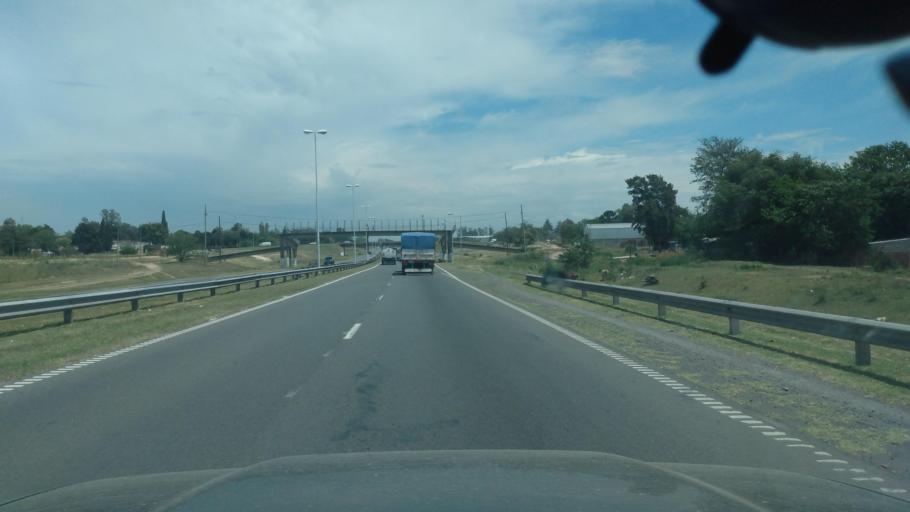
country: AR
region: Buenos Aires
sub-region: Partido de Lujan
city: Lujan
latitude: -34.5477
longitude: -59.1192
